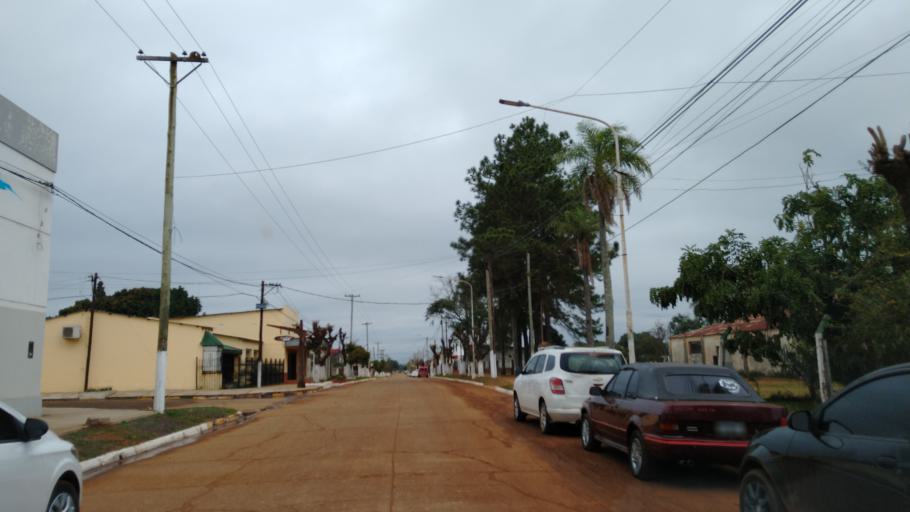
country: AR
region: Corrientes
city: Alvear
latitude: -29.0904
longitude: -56.5470
